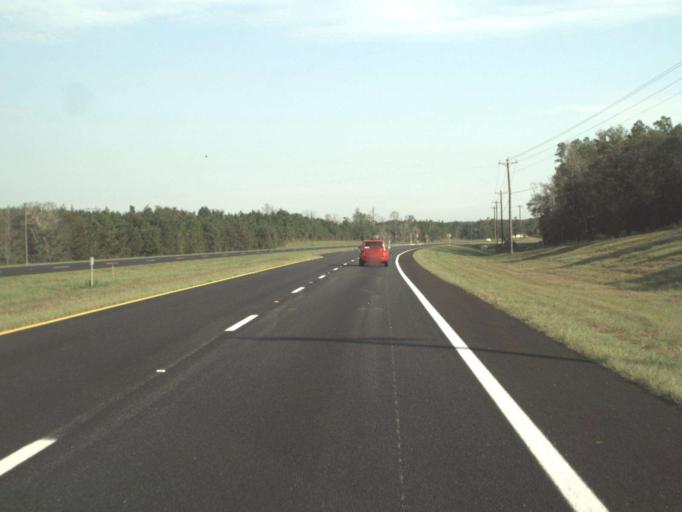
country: US
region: Florida
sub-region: Bay County
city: Laguna Beach
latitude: 30.5148
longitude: -85.8417
